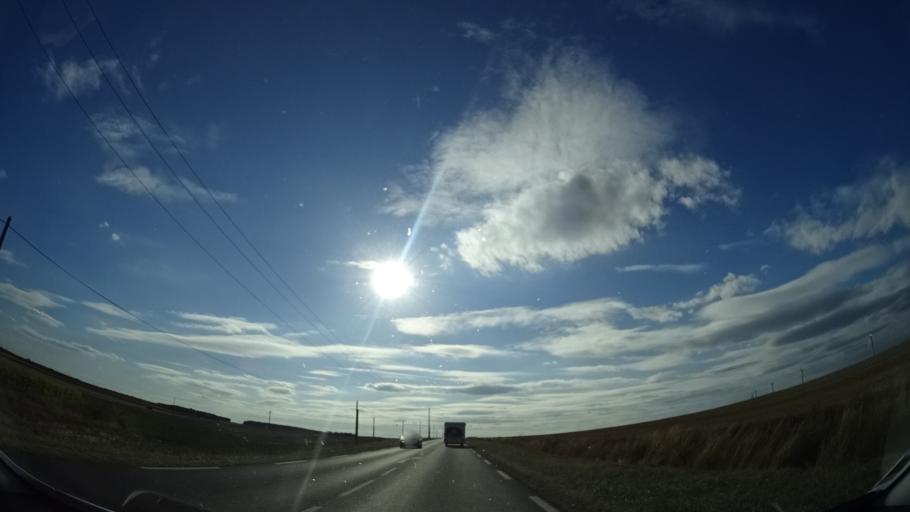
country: FR
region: Centre
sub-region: Departement du Loir-et-Cher
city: Oucques
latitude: 47.9043
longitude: 1.3719
